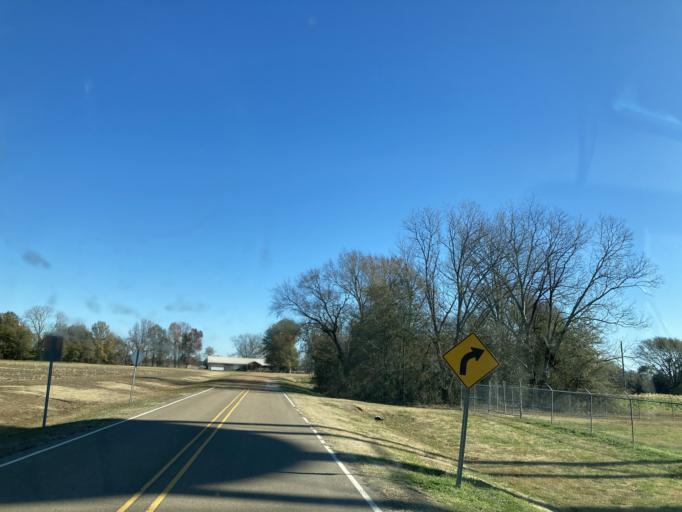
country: US
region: Mississippi
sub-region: Yazoo County
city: Yazoo City
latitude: 32.9232
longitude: -90.4927
